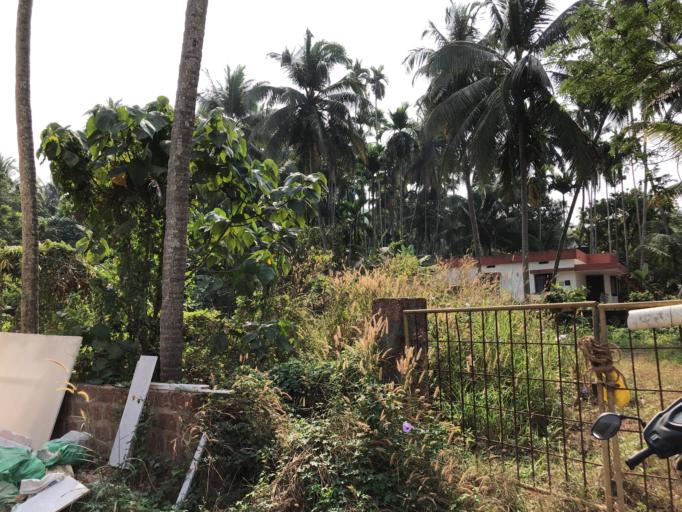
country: IN
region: Karnataka
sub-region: Dakshina Kannada
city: Mangalore
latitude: 12.8692
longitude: 74.8926
